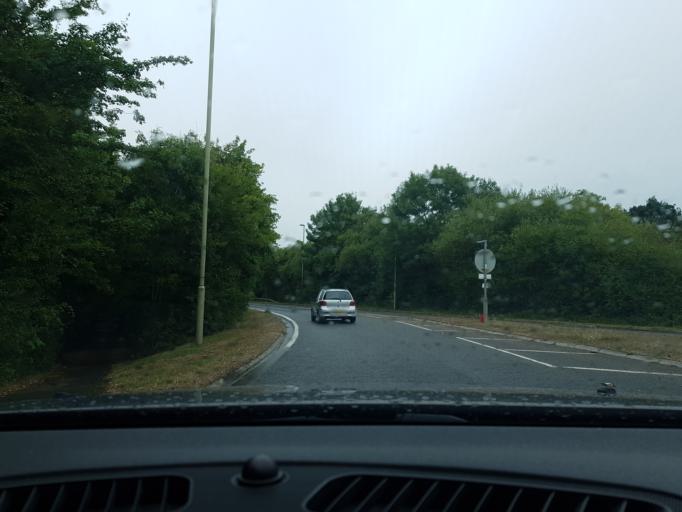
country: GB
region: England
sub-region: Hampshire
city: Odiham
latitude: 51.2566
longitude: -0.9261
